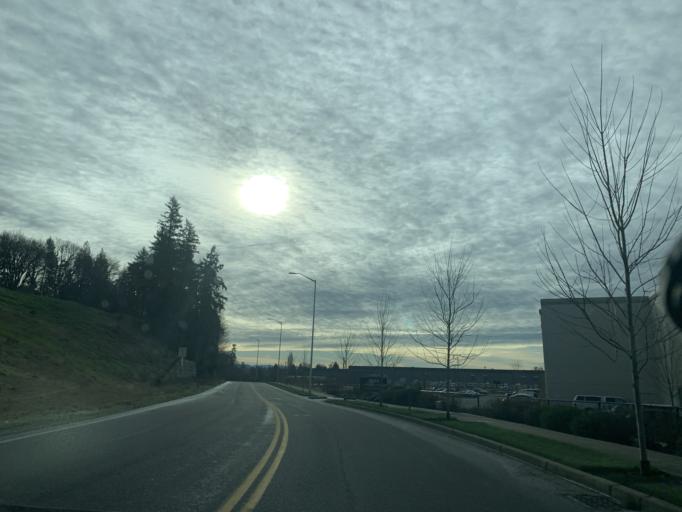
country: US
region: Washington
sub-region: Pierce County
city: Milton
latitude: 47.2320
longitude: -122.3239
